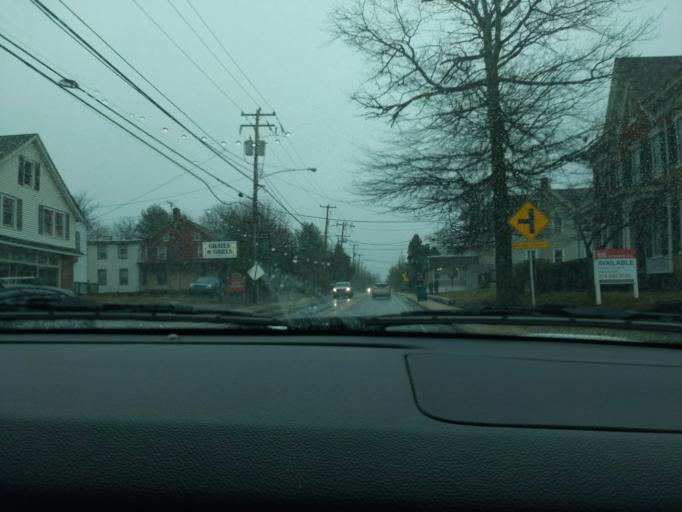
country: US
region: Pennsylvania
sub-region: Bucks County
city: Dublin
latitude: 40.3715
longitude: -75.2027
